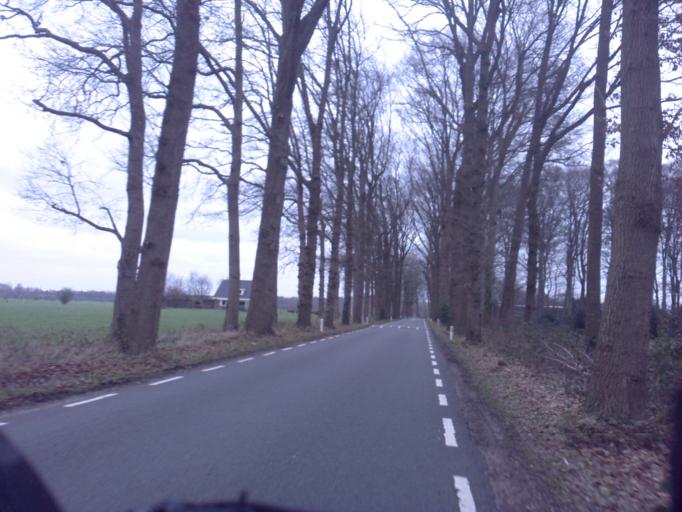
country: NL
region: Utrecht
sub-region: Gemeente Leusden
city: Leusden
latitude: 52.1532
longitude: 5.4497
